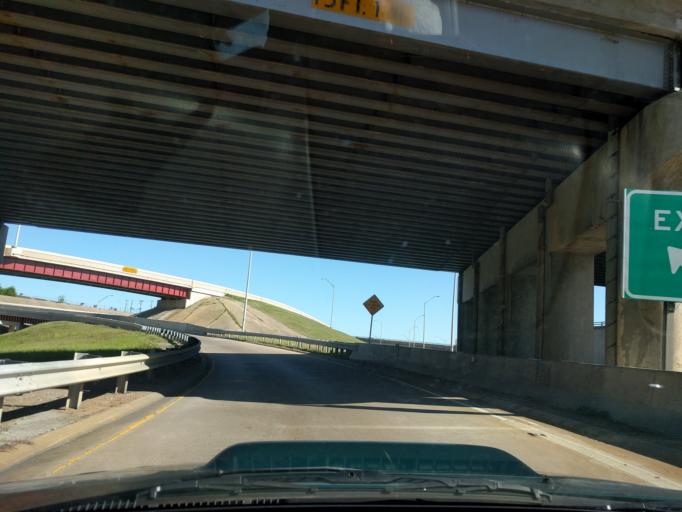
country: US
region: Oklahoma
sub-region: Tulsa County
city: Tulsa
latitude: 36.1603
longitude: -95.9803
